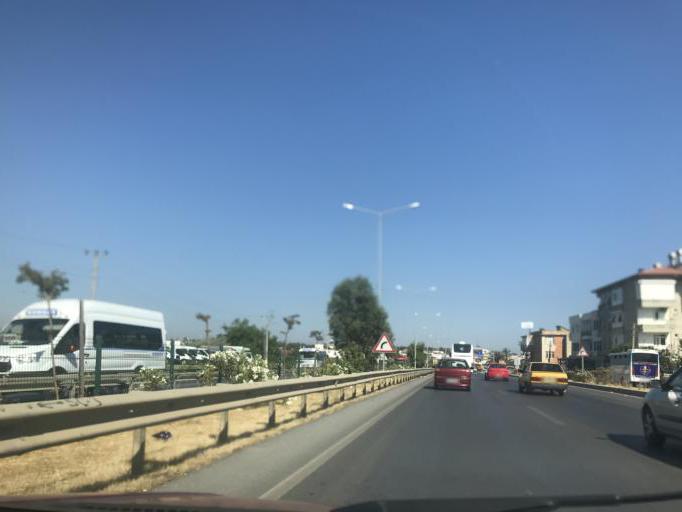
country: TR
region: Antalya
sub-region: Manavgat
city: Side
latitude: 36.7997
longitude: 31.4035
